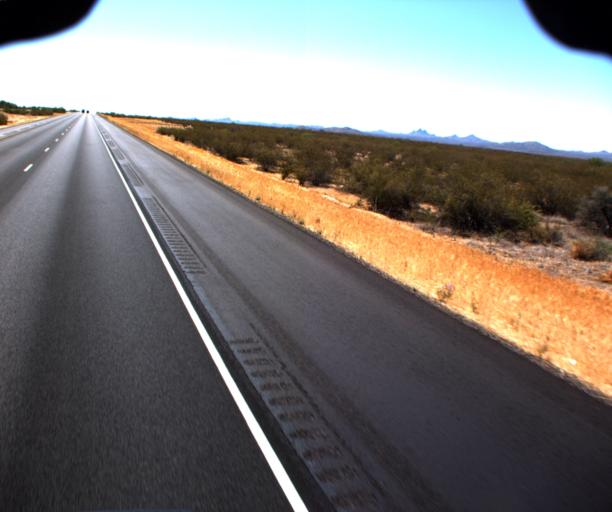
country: US
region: Arizona
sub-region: Yavapai County
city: Congress
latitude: 34.0740
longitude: -112.8801
